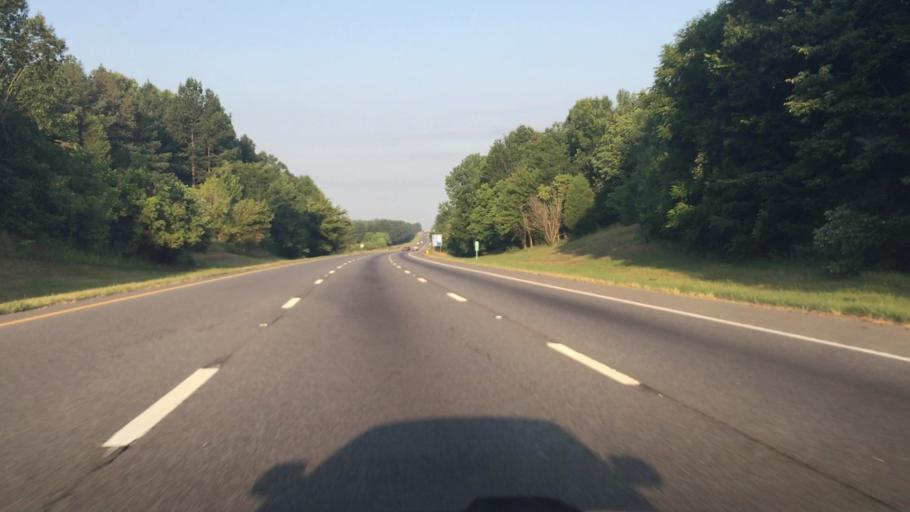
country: US
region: North Carolina
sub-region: Davidson County
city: Lexington
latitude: 35.7891
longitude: -80.2298
